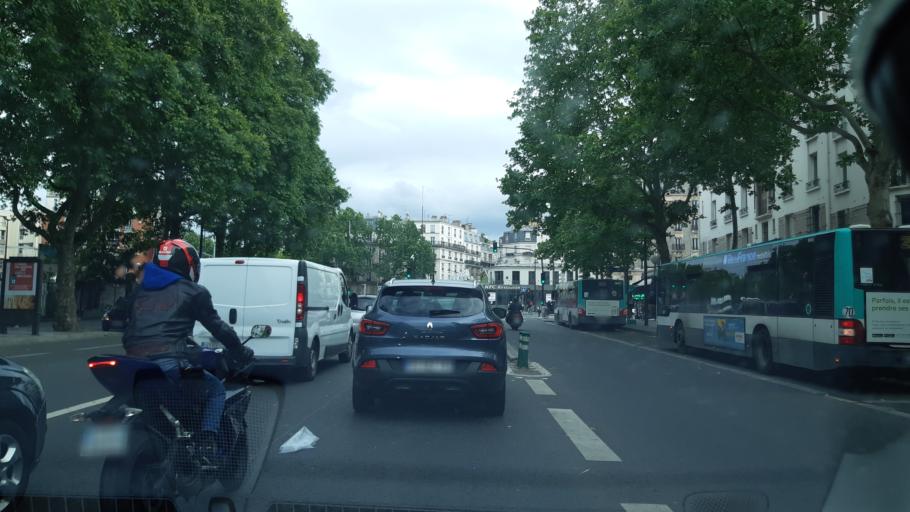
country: FR
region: Ile-de-France
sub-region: Paris
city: Saint-Ouen
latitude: 48.8988
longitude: 2.3441
